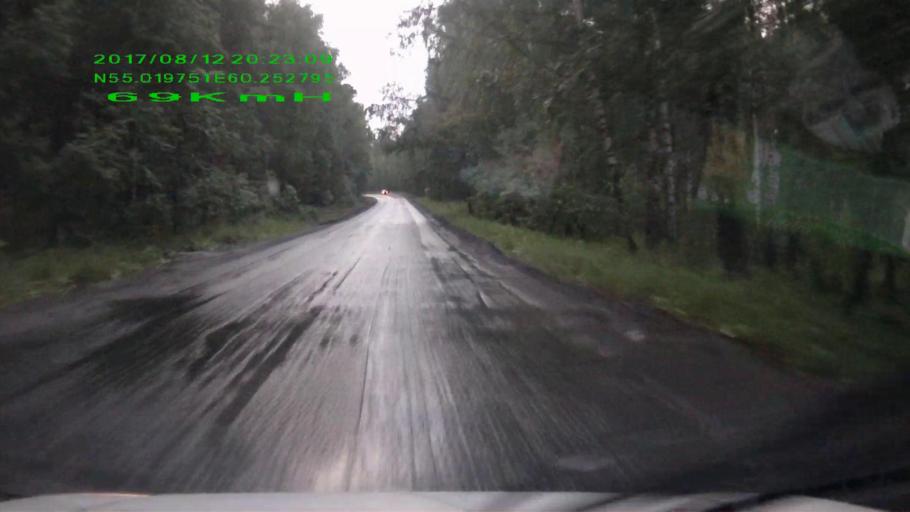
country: RU
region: Chelyabinsk
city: Chebarkul'
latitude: 55.0200
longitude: 60.2525
